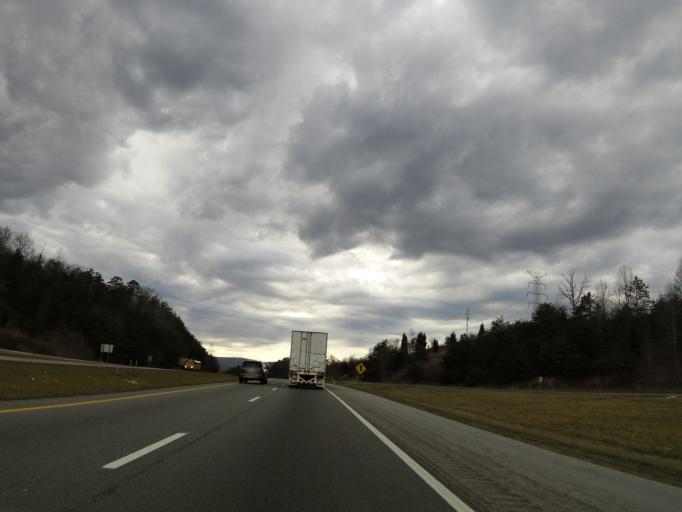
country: US
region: Tennessee
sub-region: Roane County
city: Rockwood
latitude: 35.8969
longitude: -84.7009
